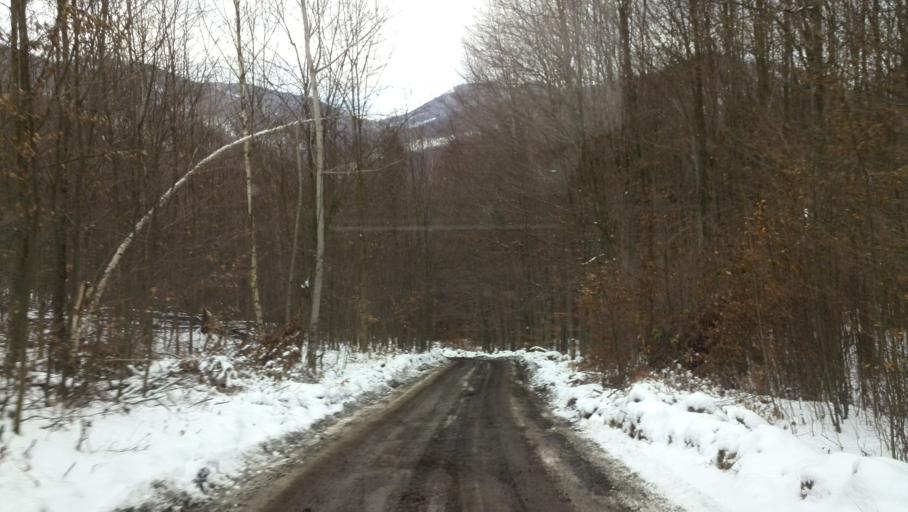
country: SK
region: Kosicky
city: Gelnica
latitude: 48.8164
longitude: 21.0694
